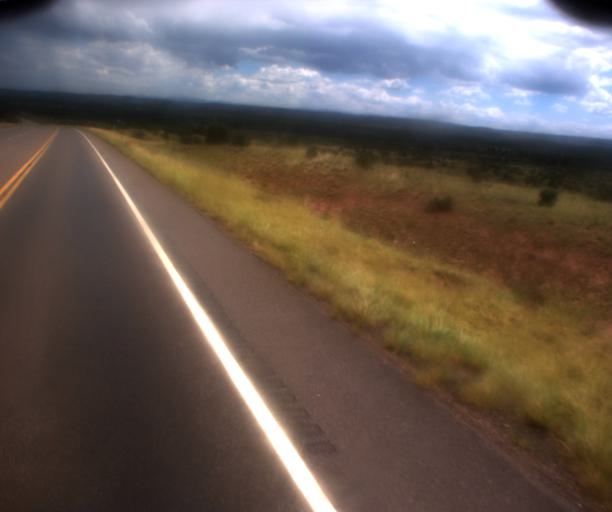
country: US
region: Arizona
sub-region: Navajo County
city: Linden
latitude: 34.3653
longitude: -110.3560
